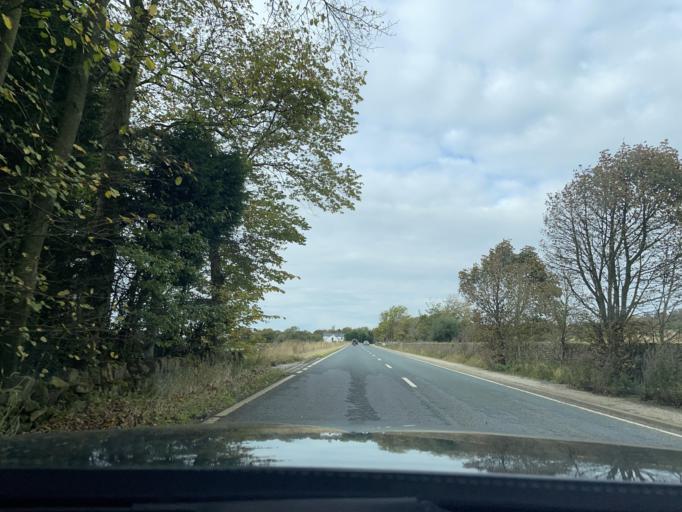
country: GB
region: England
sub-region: Sheffield
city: Bradfield
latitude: 53.3869
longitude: -1.6282
